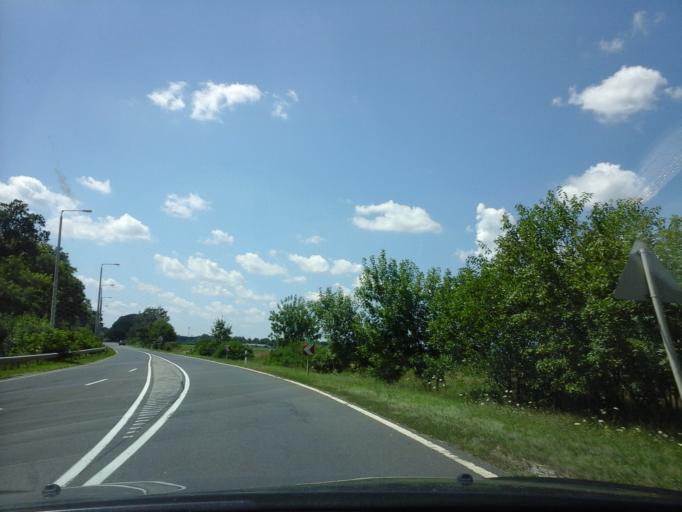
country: HU
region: Hajdu-Bihar
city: Hajduszoboszlo
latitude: 47.4610
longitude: 21.4400
